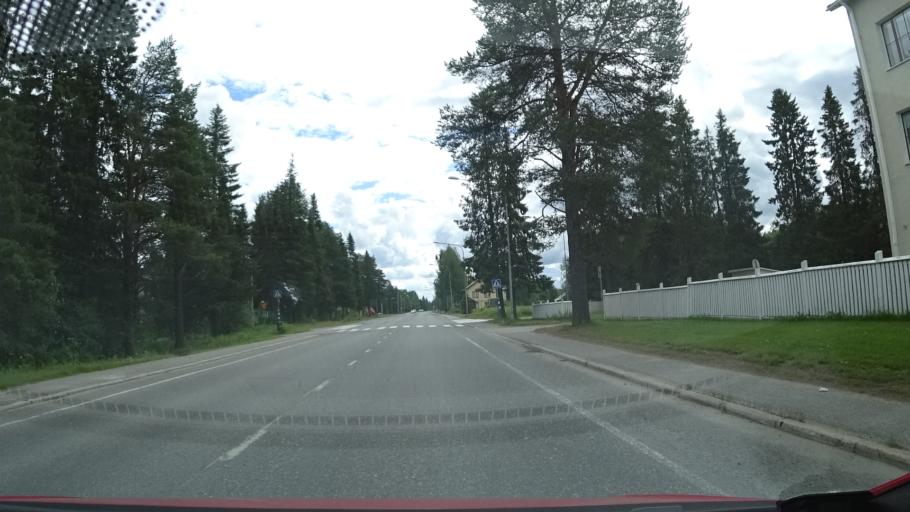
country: FI
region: Lapland
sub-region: Tunturi-Lappi
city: Kittilae
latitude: 67.6512
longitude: 24.9153
